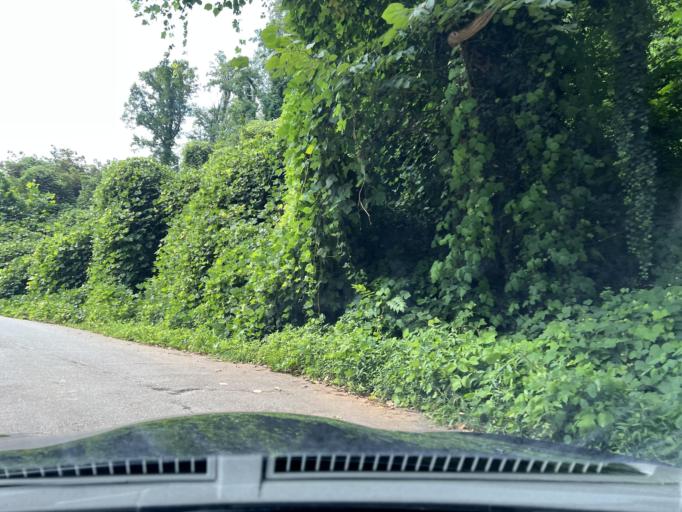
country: US
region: North Carolina
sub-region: Buncombe County
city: Asheville
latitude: 35.5731
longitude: -82.5394
